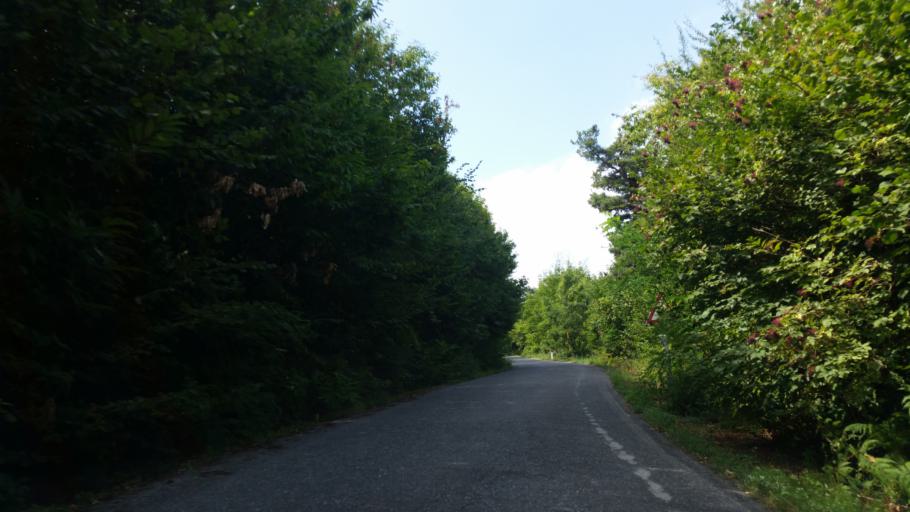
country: IT
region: Piedmont
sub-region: Provincia di Asti
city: Vesime
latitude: 44.6587
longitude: 8.2223
